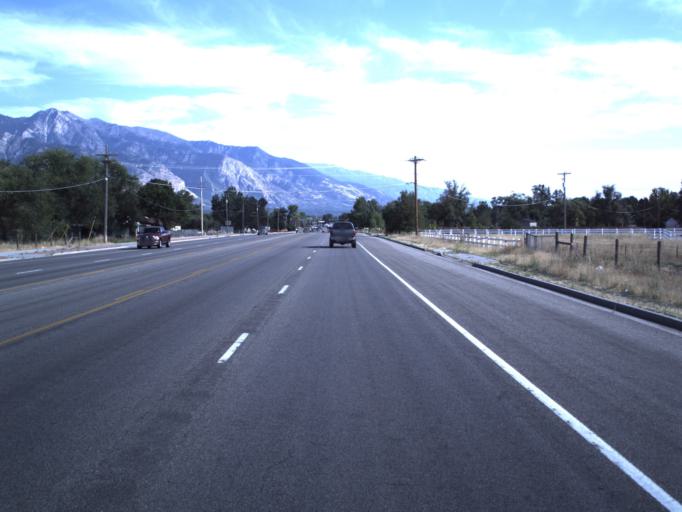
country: US
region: Utah
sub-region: Weber County
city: Harrisville
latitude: 41.2859
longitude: -111.9888
